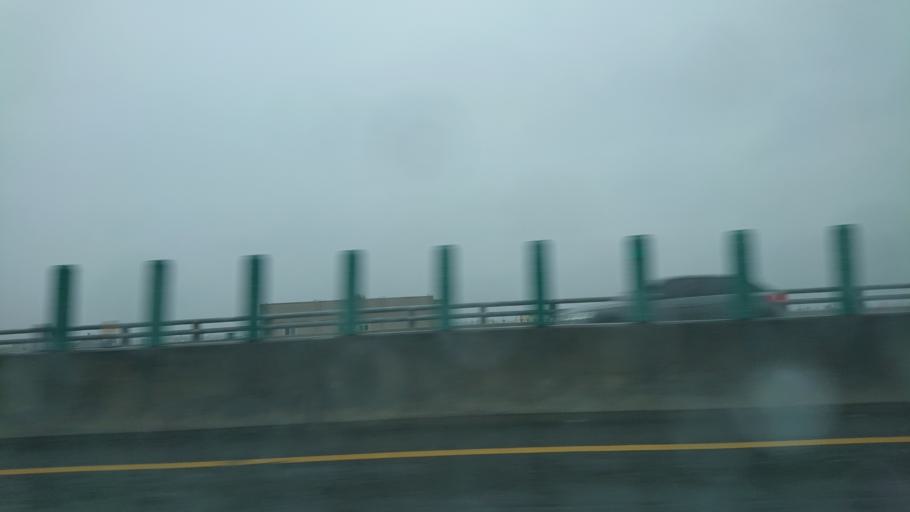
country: TW
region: Taiwan
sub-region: Changhua
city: Chang-hua
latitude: 23.9978
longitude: 120.3790
